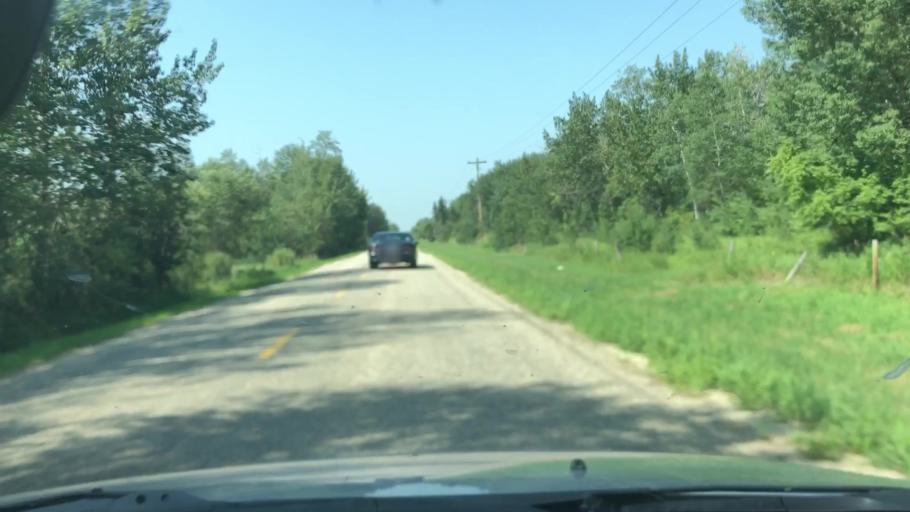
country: CA
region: Alberta
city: Devon
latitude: 53.4253
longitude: -113.7934
